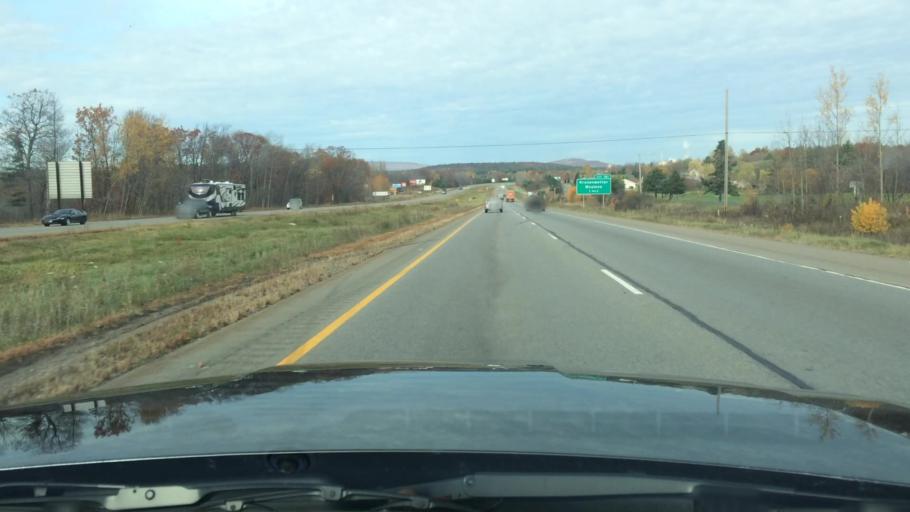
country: US
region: Wisconsin
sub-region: Marathon County
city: Mosinee
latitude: 44.7927
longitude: -89.6799
